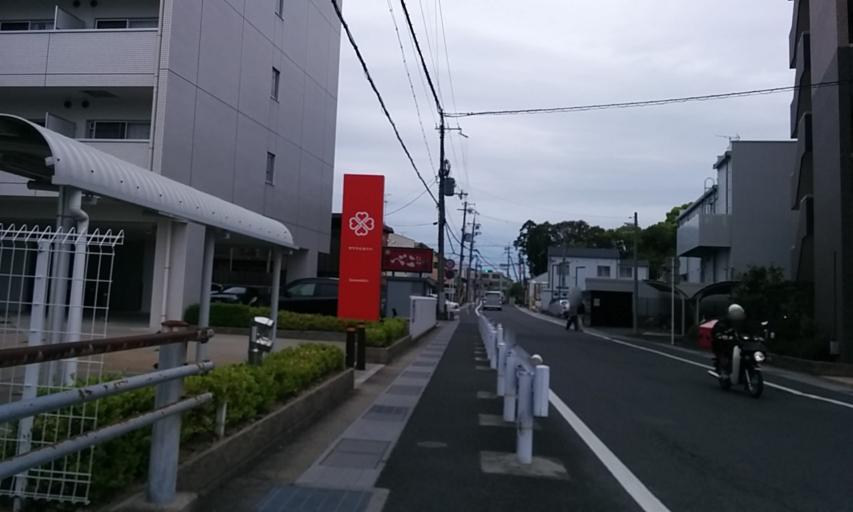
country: JP
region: Shiga Prefecture
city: Kusatsu
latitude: 35.0049
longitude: 135.9524
